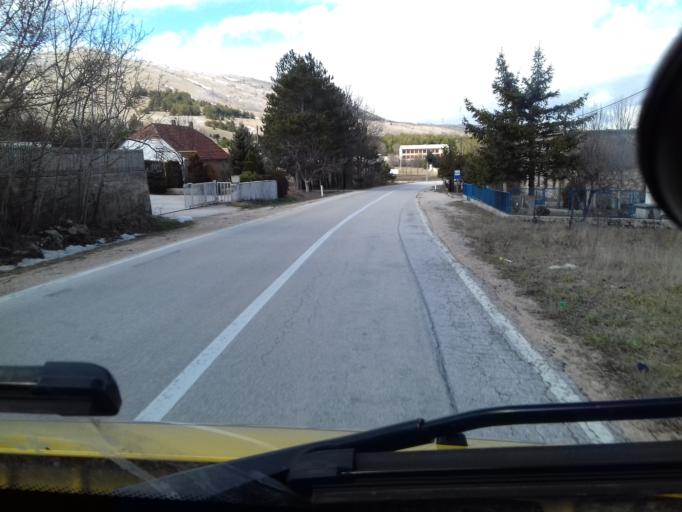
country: BA
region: Federation of Bosnia and Herzegovina
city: Dreznica
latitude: 43.5876
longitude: 17.2781
